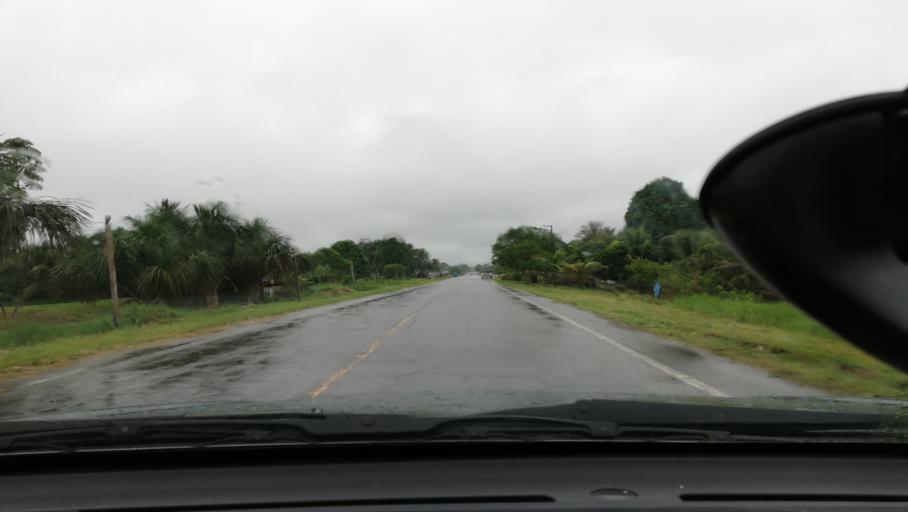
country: PE
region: Loreto
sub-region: Provincia de Maynas
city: San Juan
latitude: -4.0961
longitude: -73.4541
